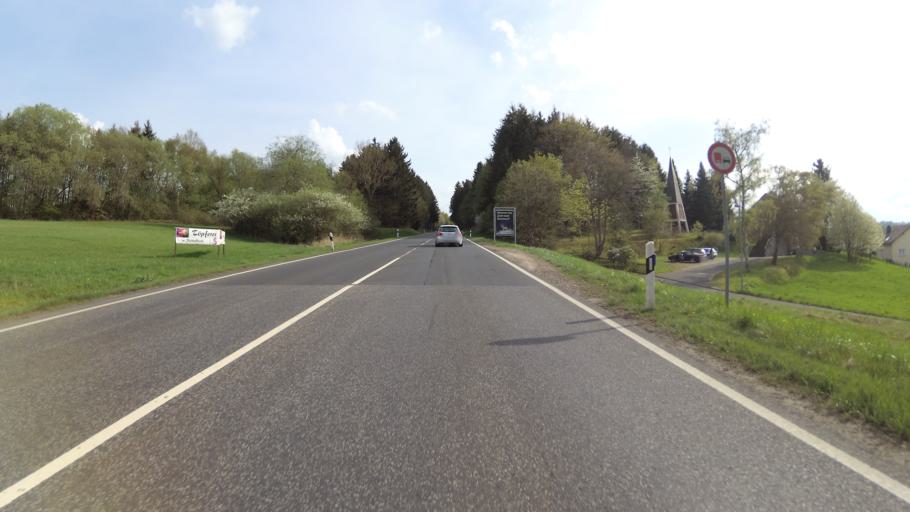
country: DE
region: Rheinland-Pfalz
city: Kelberg
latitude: 50.2841
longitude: 6.9224
